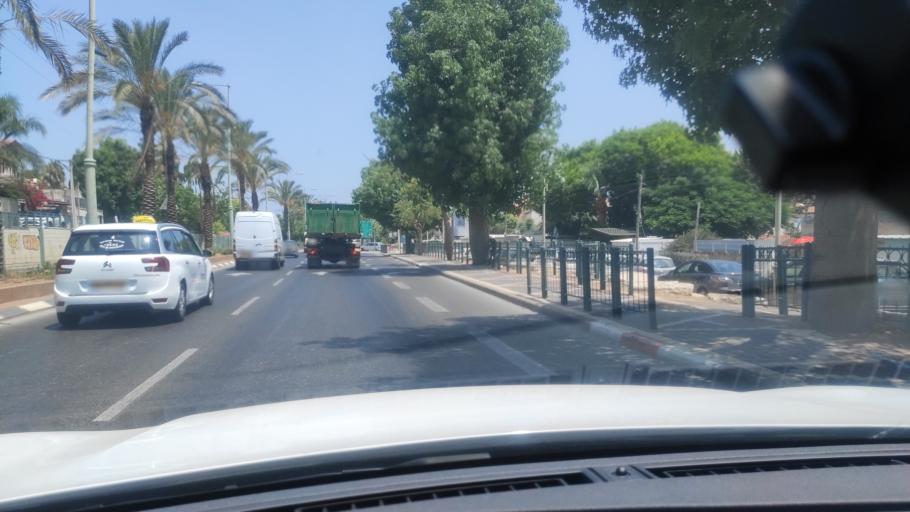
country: IL
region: Central District
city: Petah Tiqwa
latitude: 32.0934
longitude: 34.9021
